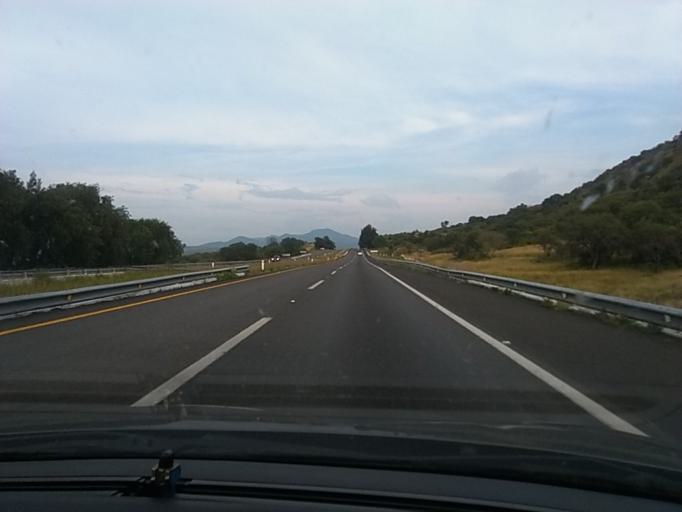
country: MX
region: Michoacan
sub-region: Zinapecuaro
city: Jose Maria Morelos (La Yegueeria)
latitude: 19.9007
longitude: -100.8525
